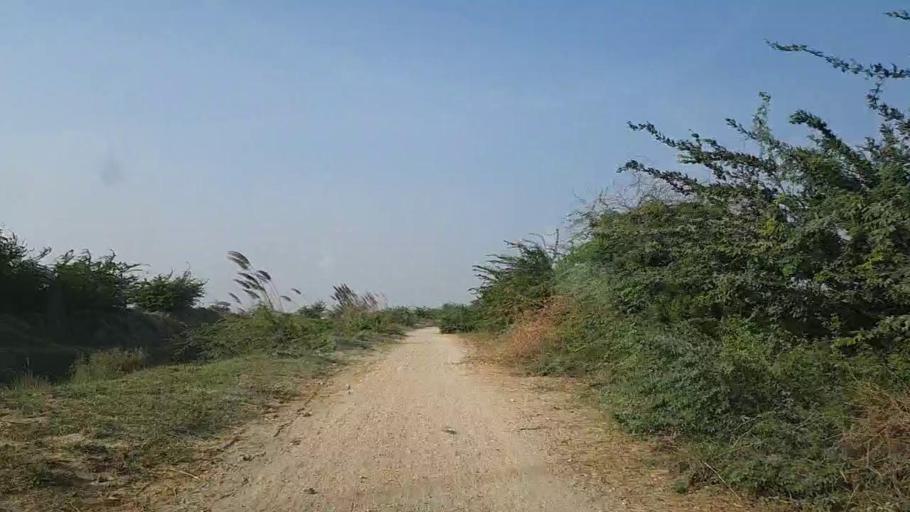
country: PK
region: Sindh
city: Mirpur Sakro
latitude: 24.5929
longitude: 67.6488
